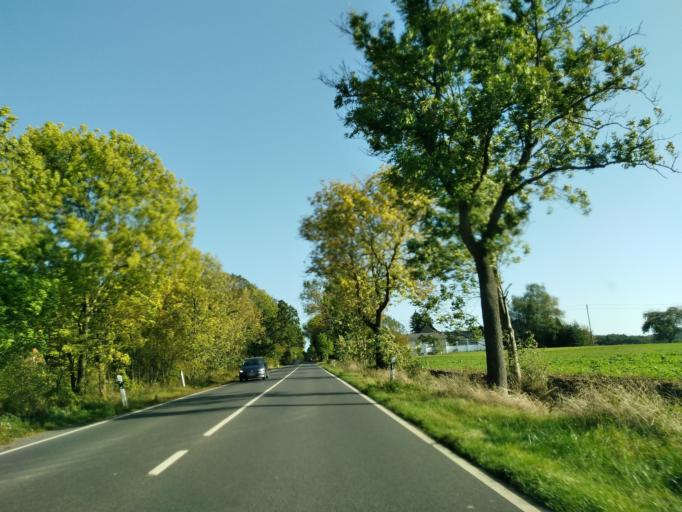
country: DE
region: Rheinland-Pfalz
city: Asbach
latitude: 50.7212
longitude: 7.3810
